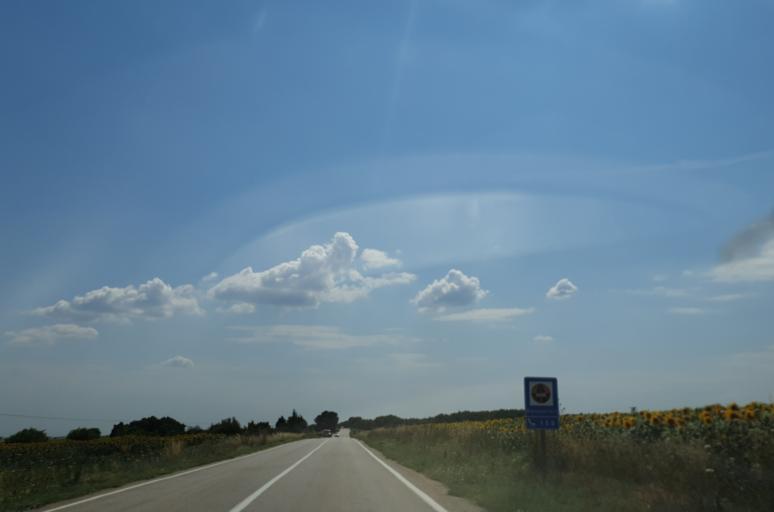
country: TR
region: Kirklareli
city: Vize
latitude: 41.4801
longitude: 27.6817
